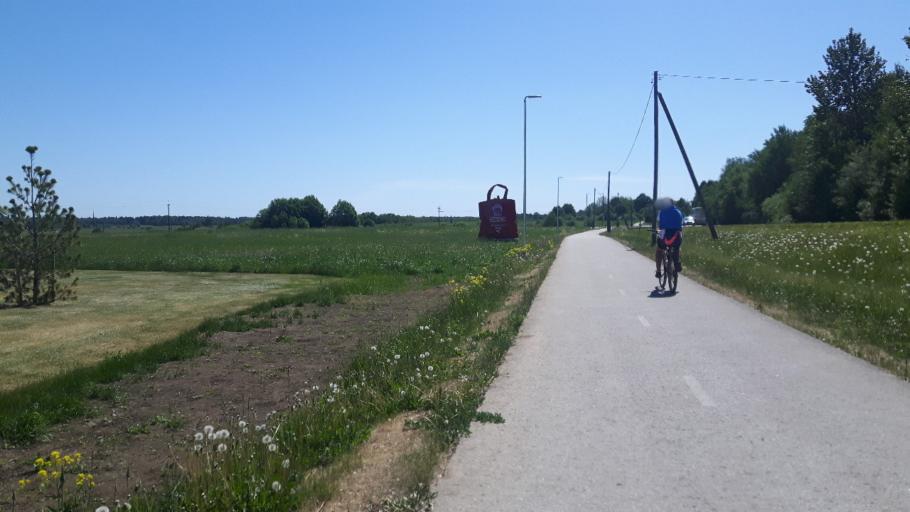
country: EE
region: Harju
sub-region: Saku vald
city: Saku
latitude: 59.2912
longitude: 24.6597
